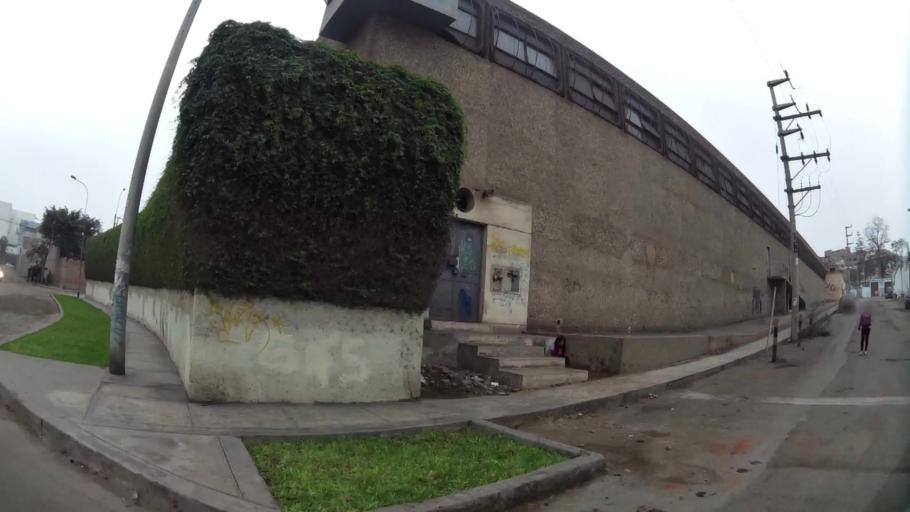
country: PE
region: Lima
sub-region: Lima
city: Surco
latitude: -12.1579
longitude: -76.9795
